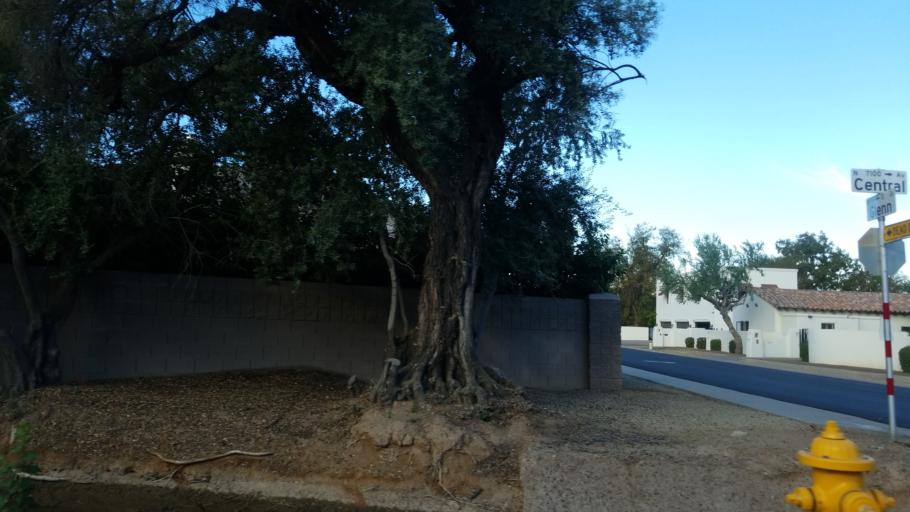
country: US
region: Arizona
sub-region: Maricopa County
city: Phoenix
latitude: 33.5403
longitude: -112.0738
